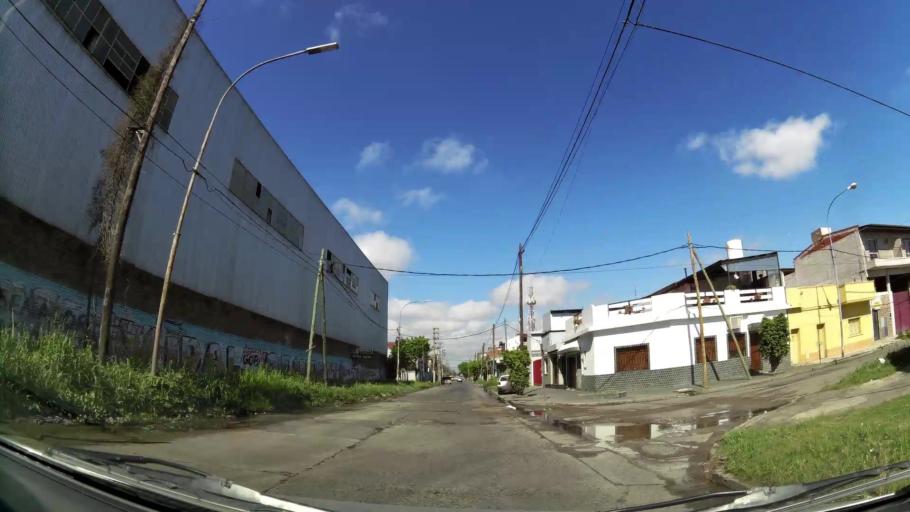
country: AR
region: Buenos Aires
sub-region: Partido de Lanus
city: Lanus
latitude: -34.6698
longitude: -58.4194
